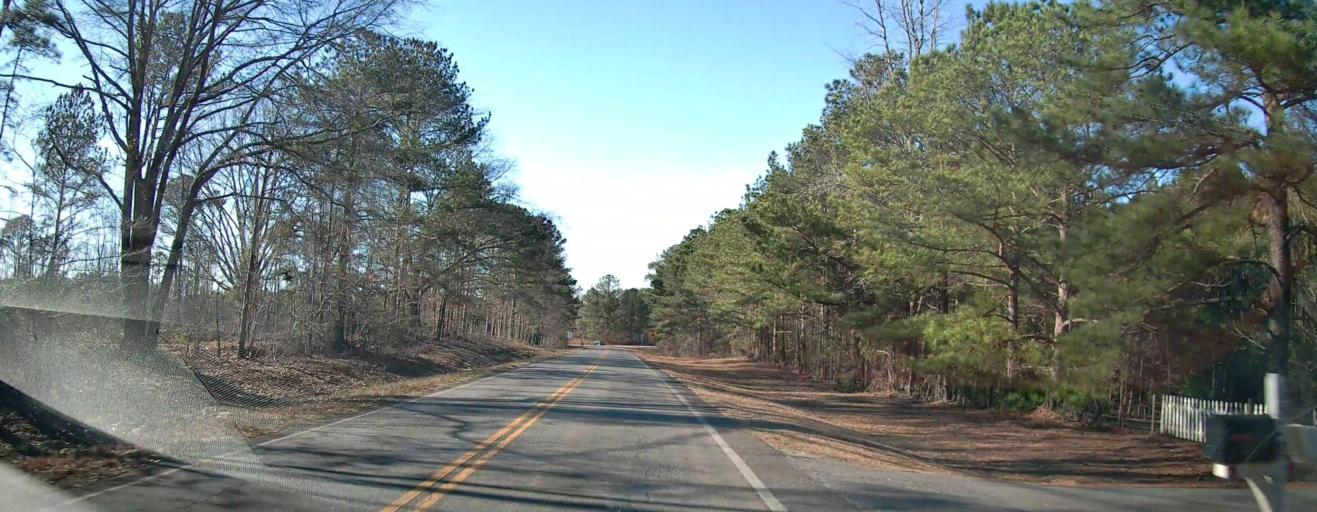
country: US
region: Georgia
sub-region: Talbot County
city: Sardis
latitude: 32.7815
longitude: -84.6856
